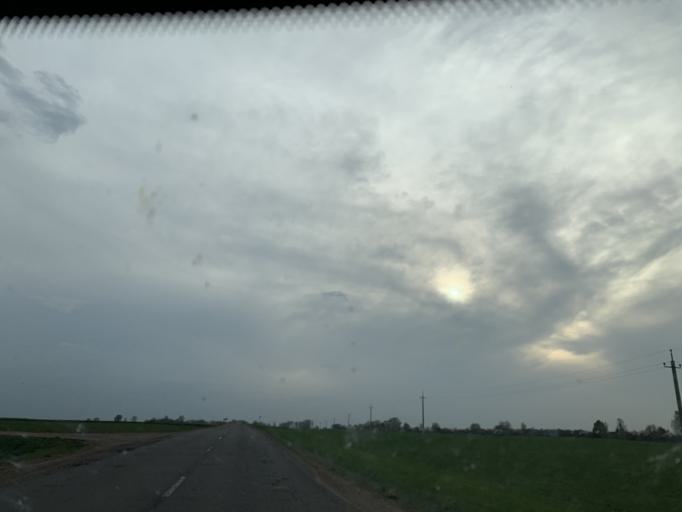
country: BY
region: Minsk
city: Kapyl'
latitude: 53.2929
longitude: 27.0277
